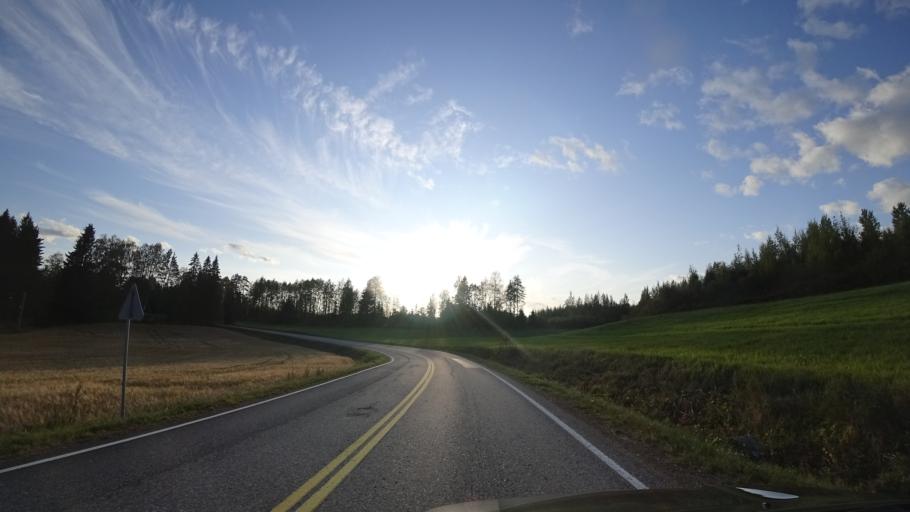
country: FI
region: Haeme
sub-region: Haemeenlinna
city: Lammi
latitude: 61.0615
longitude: 24.9726
